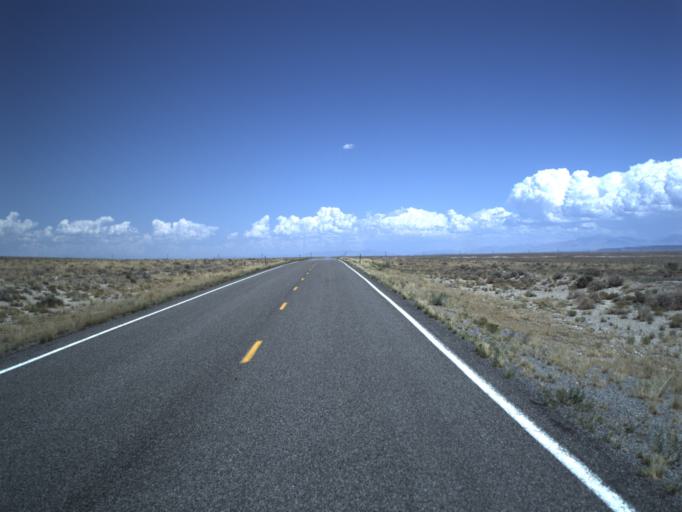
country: US
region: Utah
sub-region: Millard County
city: Delta
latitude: 39.1505
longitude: -113.0688
